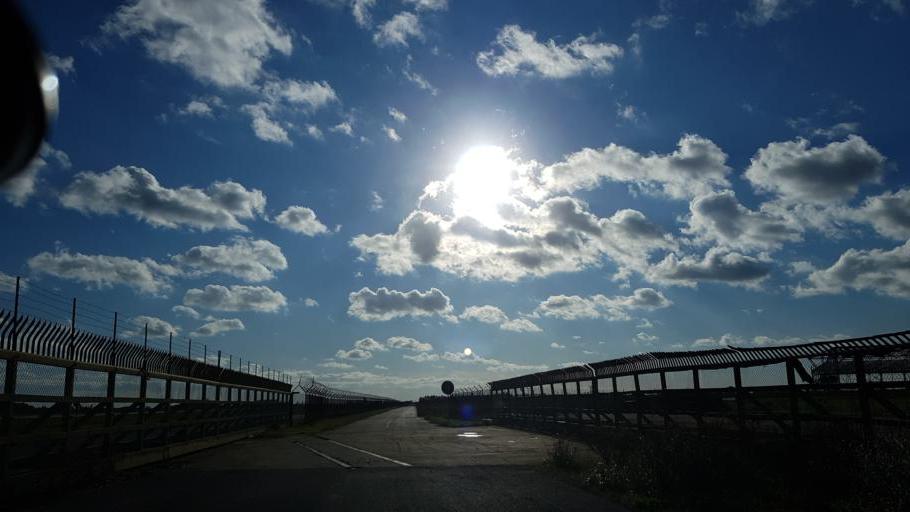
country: IT
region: Apulia
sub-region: Provincia di Brindisi
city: Materdomini
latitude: 40.6734
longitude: 17.9255
